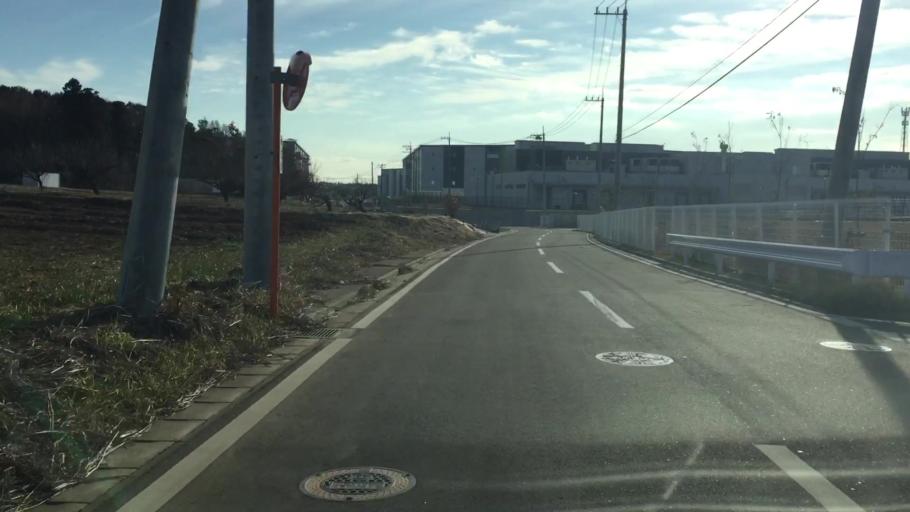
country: JP
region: Chiba
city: Shiroi
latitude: 35.8174
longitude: 140.1267
